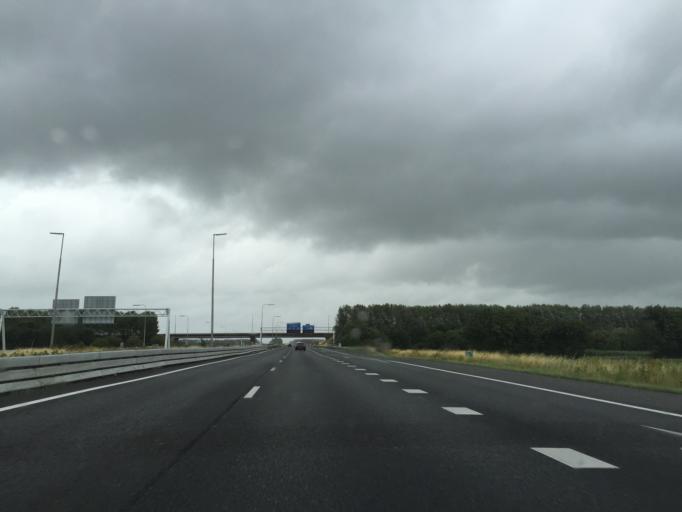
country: NL
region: Flevoland
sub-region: Gemeente Almere
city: Almere Stad
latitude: 52.3857
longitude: 5.3107
